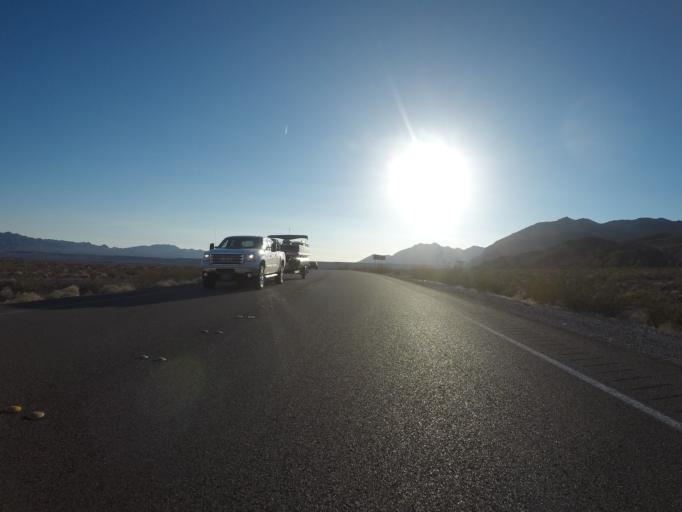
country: US
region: Nevada
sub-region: Clark County
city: Moapa Valley
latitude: 36.3793
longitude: -114.4396
